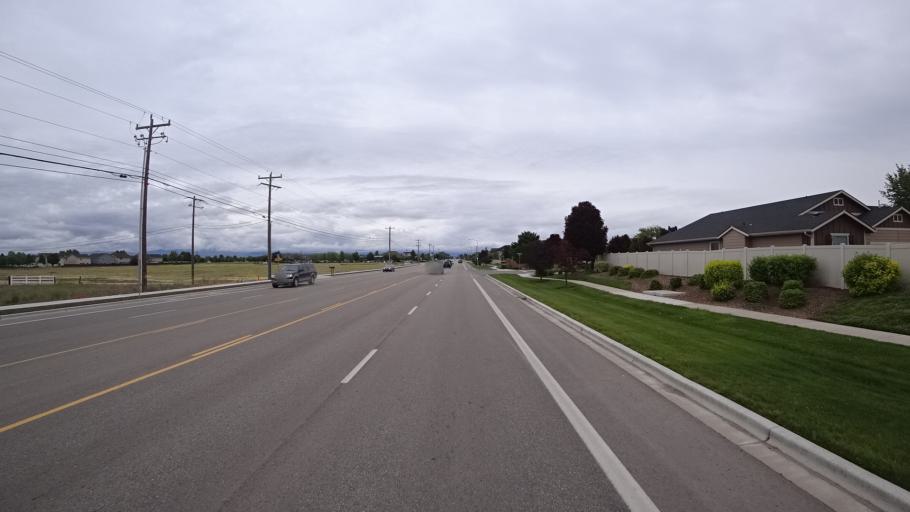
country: US
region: Idaho
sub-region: Ada County
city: Meridian
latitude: 43.6338
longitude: -116.4071
